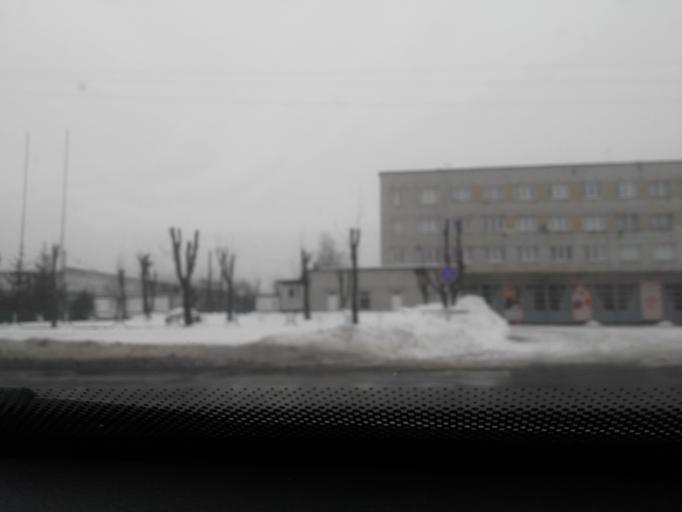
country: BY
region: Mogilev
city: Babruysk
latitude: 53.1876
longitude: 29.2118
